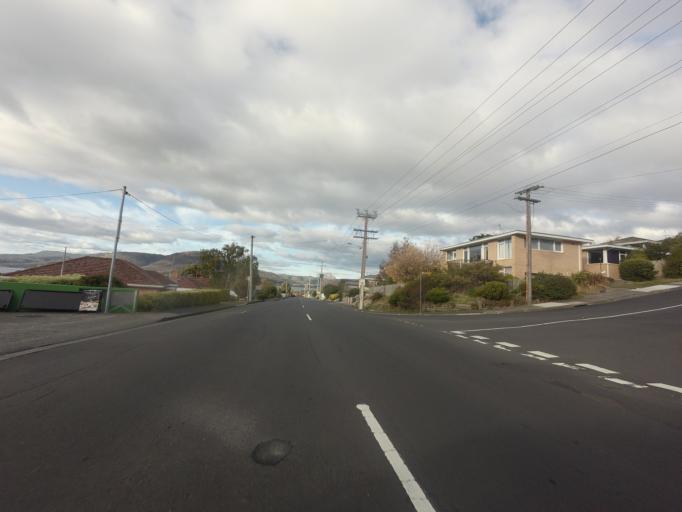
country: AU
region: Tasmania
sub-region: Glenorchy
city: Berriedale
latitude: -42.8233
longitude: 147.2566
